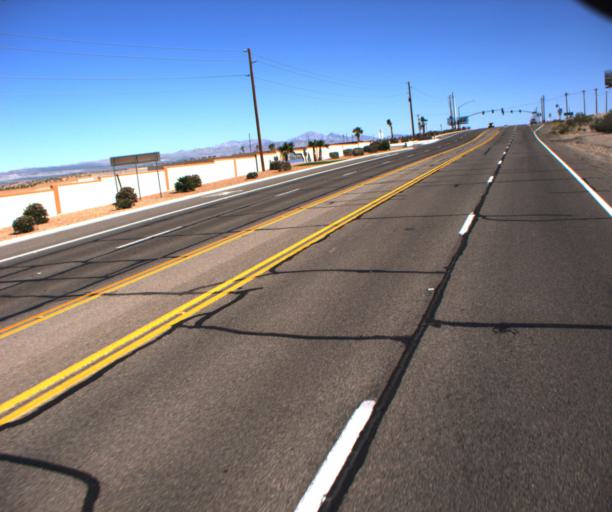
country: US
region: Arizona
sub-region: Mohave County
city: Mohave Valley
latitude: 34.9800
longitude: -114.5979
